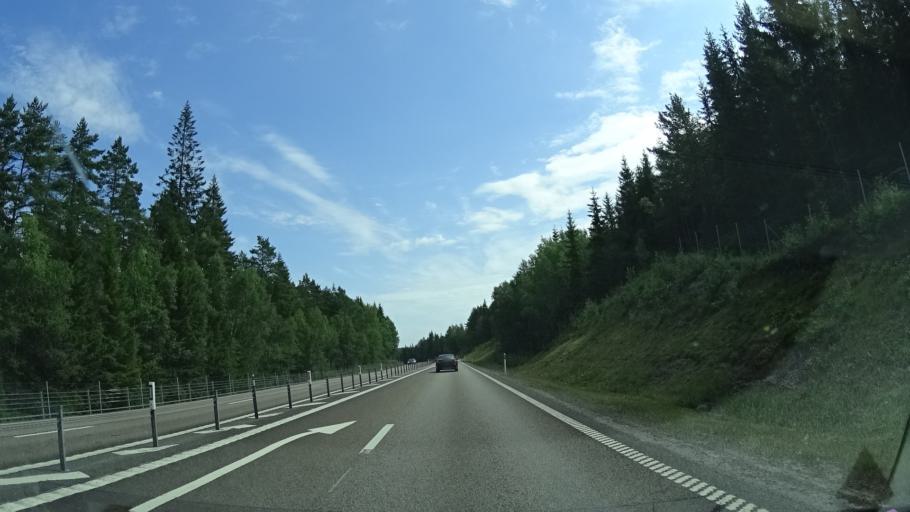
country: SE
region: Vaermland
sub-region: Kristinehamns Kommun
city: Bjorneborg
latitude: 59.3098
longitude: 14.2926
